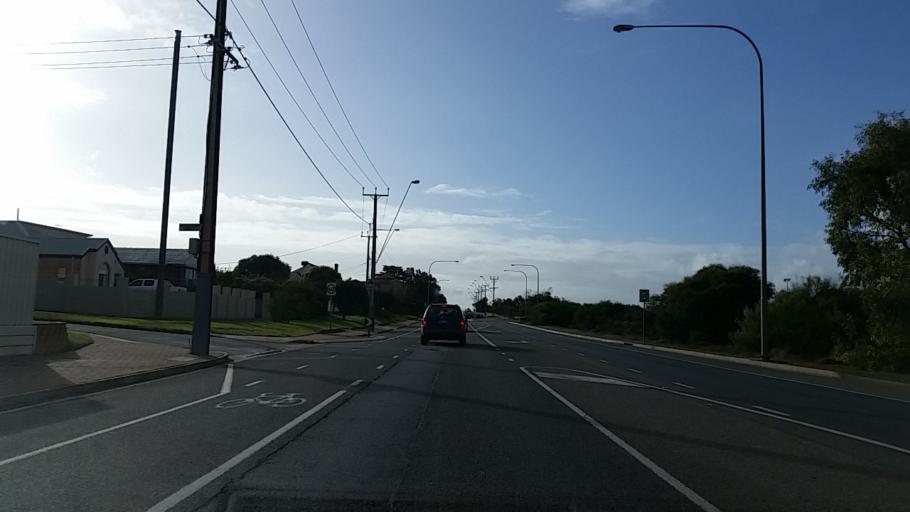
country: AU
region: South Australia
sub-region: Adelaide
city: Port Noarlunga
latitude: -35.1606
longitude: 138.4751
